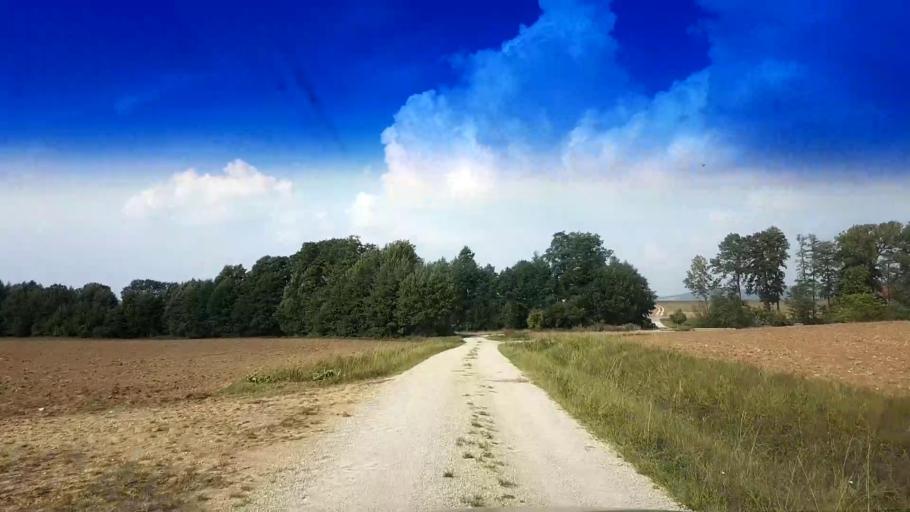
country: DE
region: Bavaria
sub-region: Upper Franconia
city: Schesslitz
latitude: 49.9536
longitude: 11.0153
